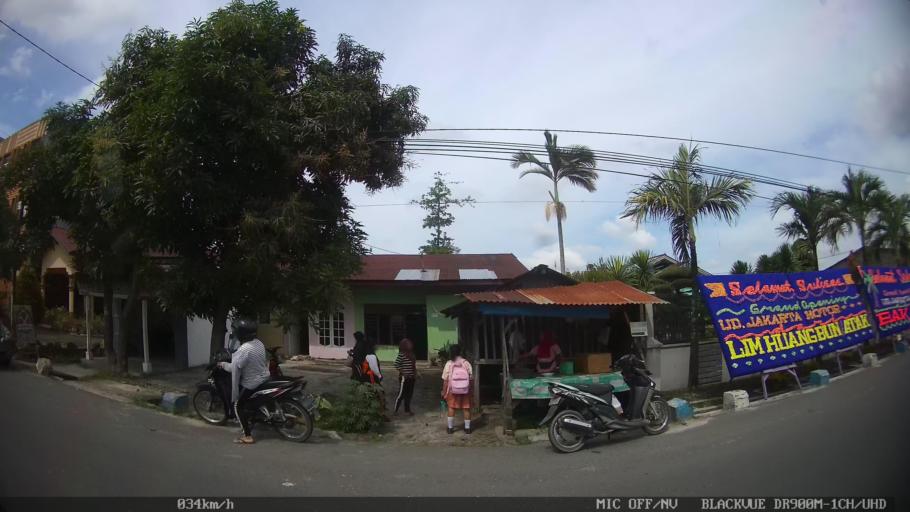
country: ID
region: North Sumatra
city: Percut
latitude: 3.5755
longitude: 98.8674
